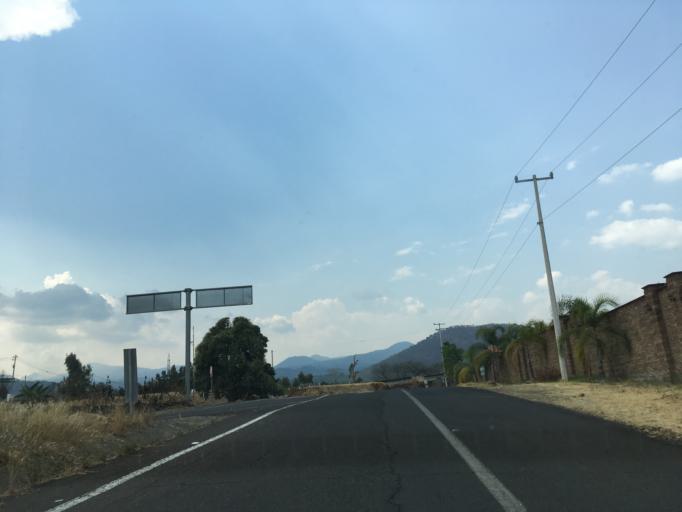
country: MX
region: Michoacan
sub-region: Ziracuaretiro
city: Patuan
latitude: 19.4228
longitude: -101.9222
